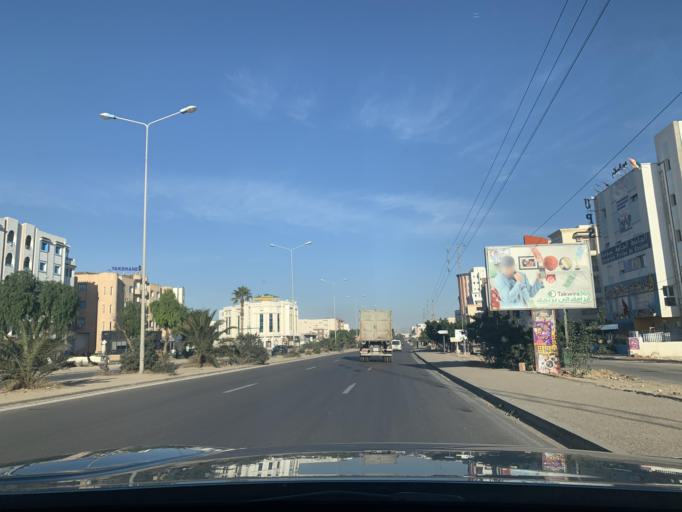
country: DZ
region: Souk Ahras
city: Souk Ahras
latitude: 36.3710
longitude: 7.9965
